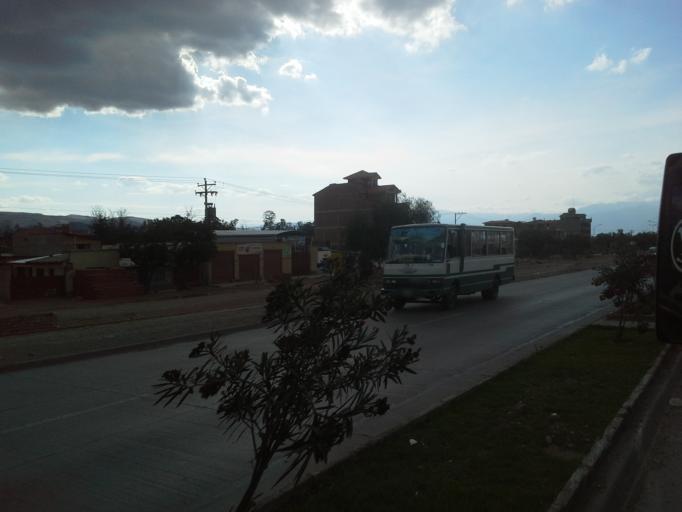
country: BO
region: Cochabamba
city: Cochabamba
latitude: -17.4452
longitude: -66.1383
